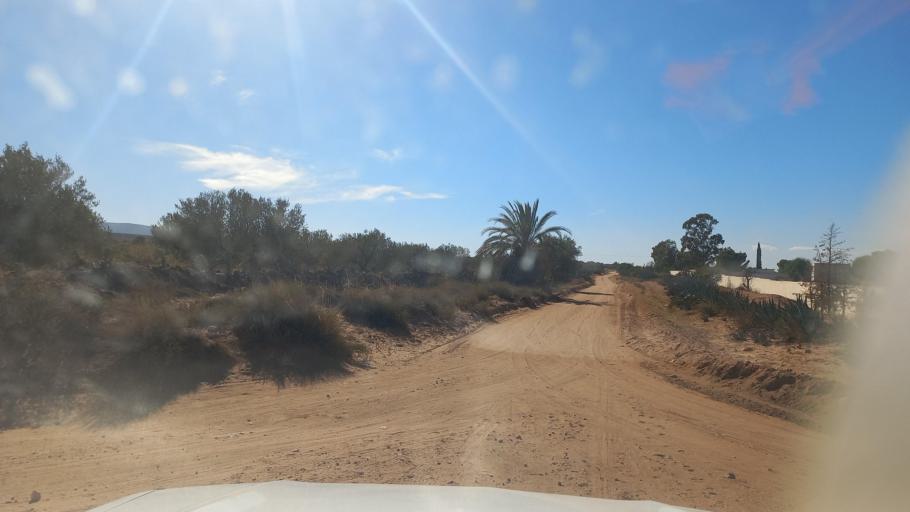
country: TN
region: Al Qasrayn
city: Kasserine
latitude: 35.2138
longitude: 8.9751
